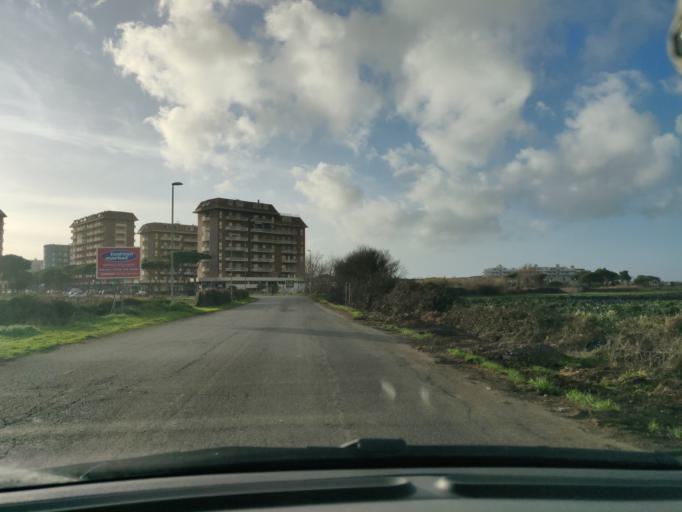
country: IT
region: Latium
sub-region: Provincia di Viterbo
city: Tarquinia
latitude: 42.2252
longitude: 11.7109
